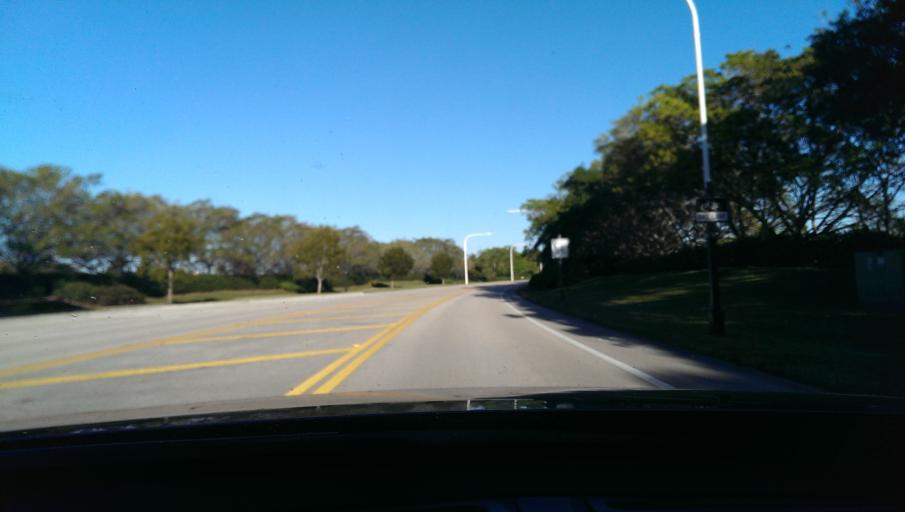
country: US
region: Florida
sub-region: Broward County
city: Weston
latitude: 26.0751
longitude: -80.3962
